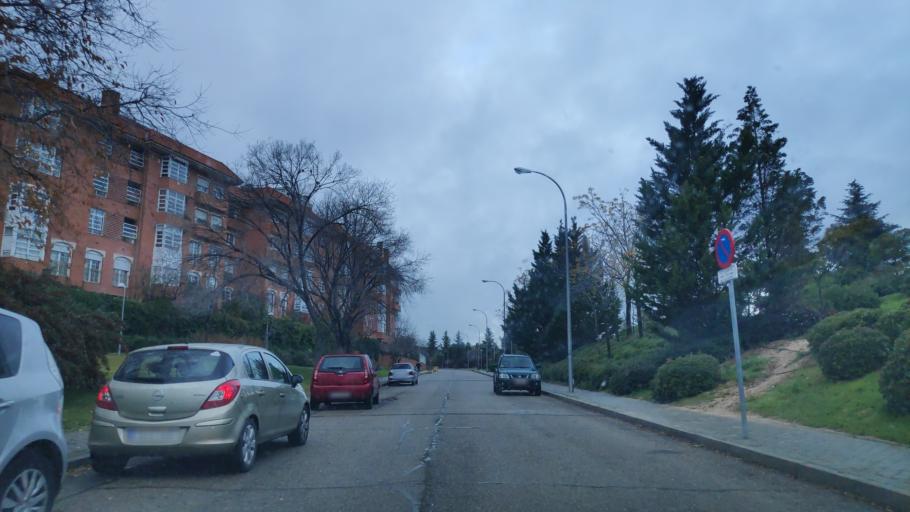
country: ES
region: Madrid
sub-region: Provincia de Madrid
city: San Blas
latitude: 40.4584
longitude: -3.6219
